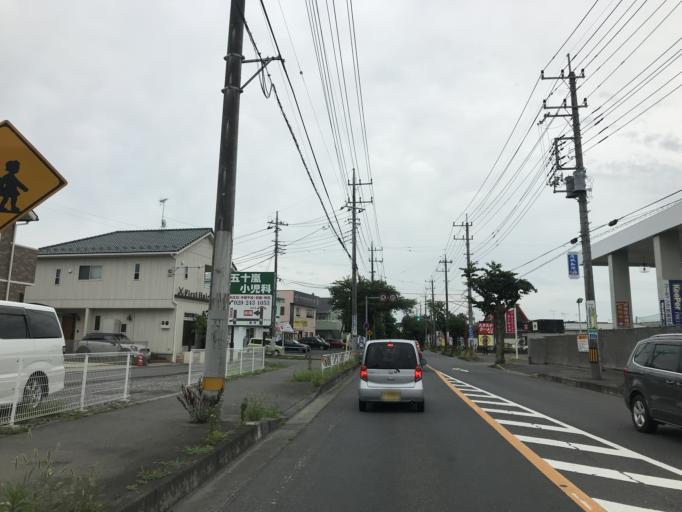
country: JP
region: Ibaraki
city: Mito-shi
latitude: 36.3359
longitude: 140.4614
